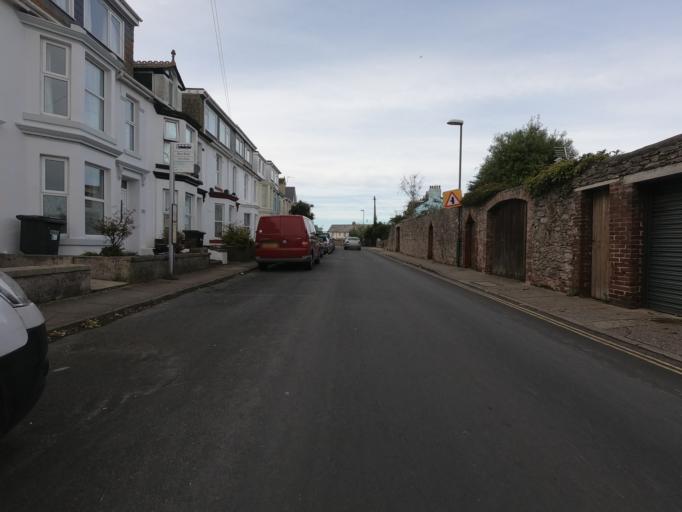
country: GB
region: England
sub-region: Borough of Torbay
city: Brixham
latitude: 50.3989
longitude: -3.5174
